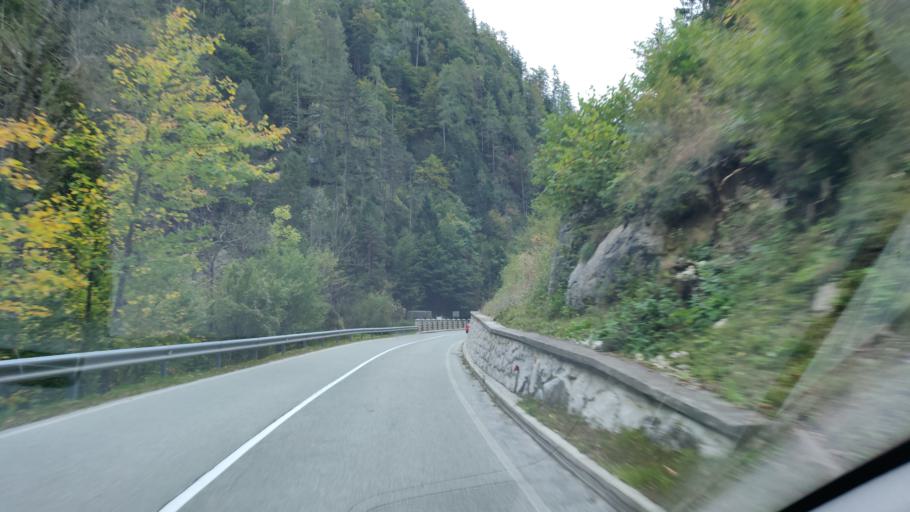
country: SI
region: Jezersko
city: Zgornje Jezersko
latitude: 46.3755
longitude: 14.4717
